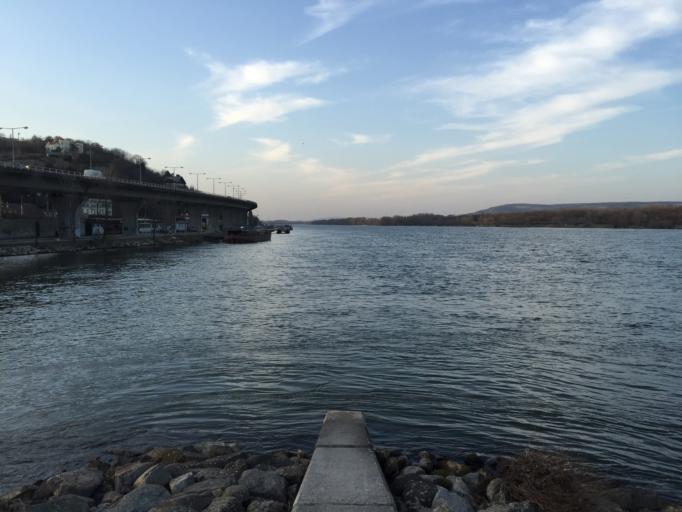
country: AT
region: Lower Austria
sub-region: Politischer Bezirk Korneuburg
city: Langenzersdorf
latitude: 48.2615
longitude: 16.3691
